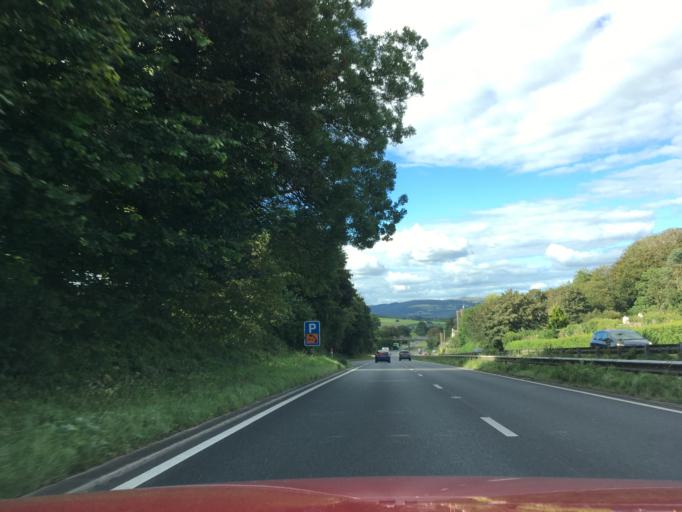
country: GB
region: England
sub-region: Devon
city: Buckfastleigh
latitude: 50.4552
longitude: -3.7908
